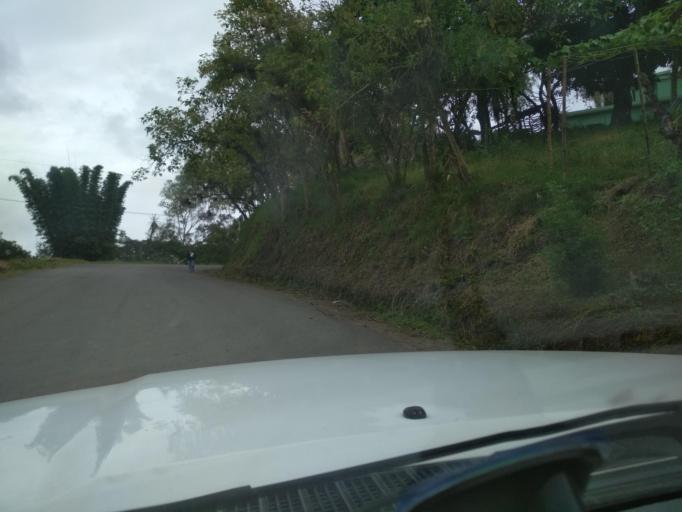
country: MX
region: Veracruz
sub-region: Emiliano Zapata
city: Dos Rios
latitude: 19.5384
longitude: -96.8020
